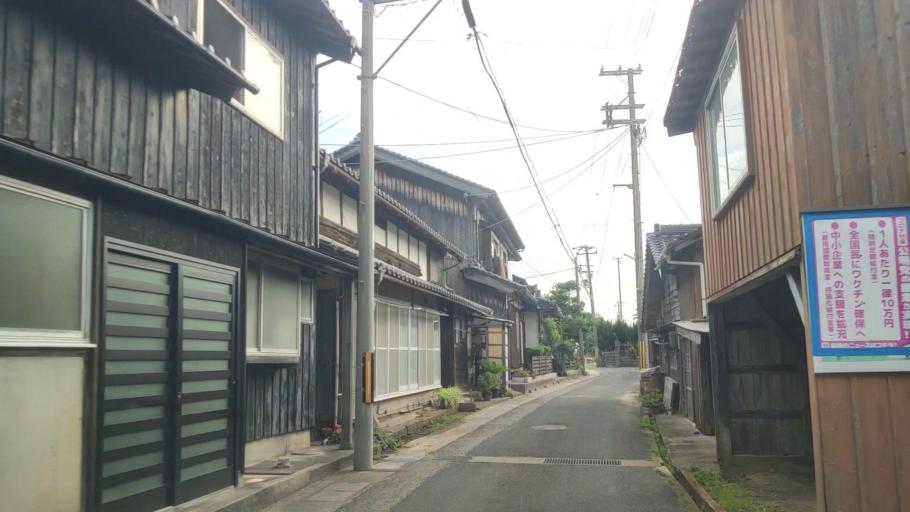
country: JP
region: Hyogo
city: Toyooka
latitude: 35.6448
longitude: 134.9014
